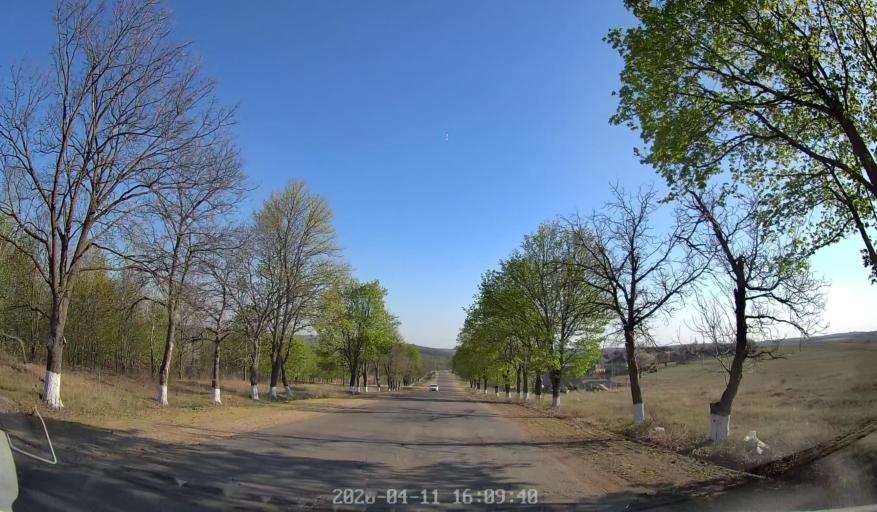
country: MD
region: Chisinau
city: Vadul lui Voda
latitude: 47.0724
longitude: 29.1368
